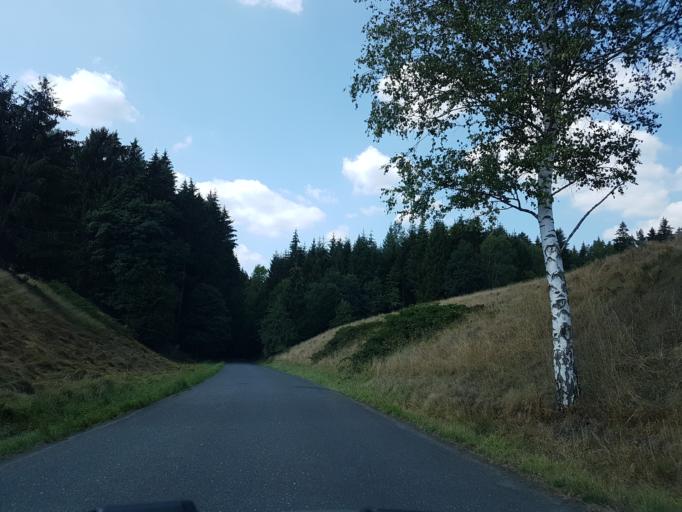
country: CZ
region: Ustecky
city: Ceska Kamenice
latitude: 50.8635
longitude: 14.3494
